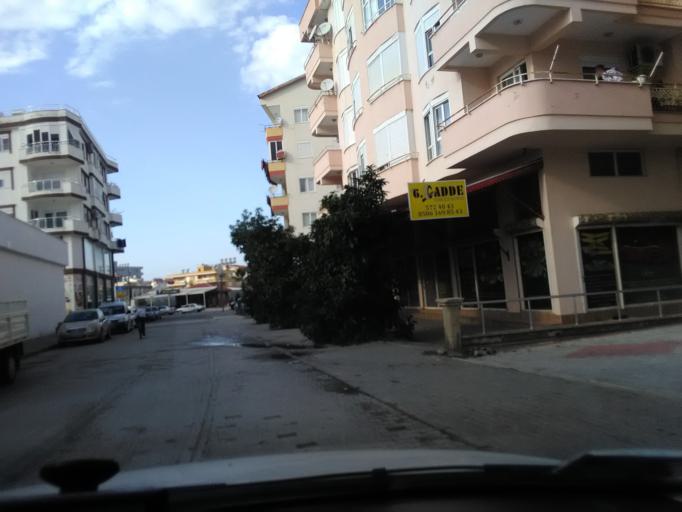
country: TR
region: Antalya
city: Gazipasa
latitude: 36.2700
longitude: 32.3200
